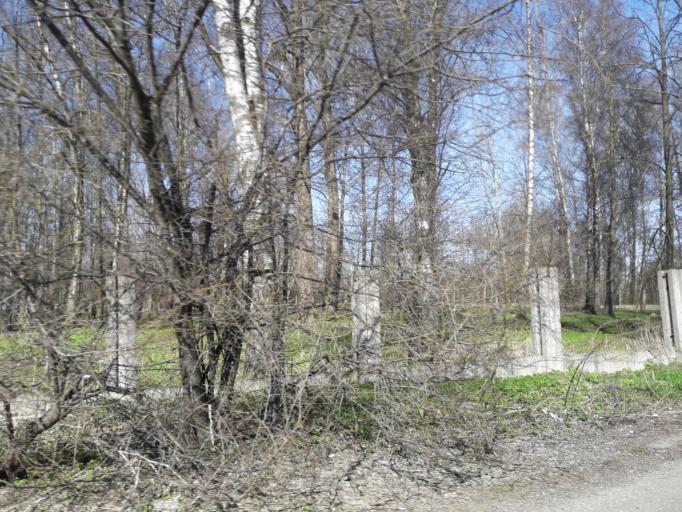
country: LT
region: Siauliu apskritis
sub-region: Siauliai
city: Siauliai
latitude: 55.9400
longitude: 23.3181
